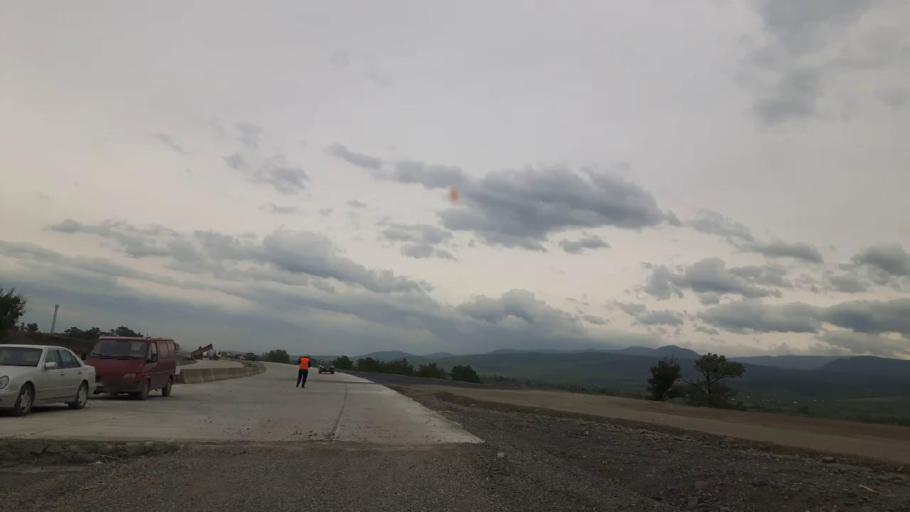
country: GE
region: Shida Kartli
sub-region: Khashuris Raioni
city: Khashuri
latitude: 42.0108
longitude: 43.7061
